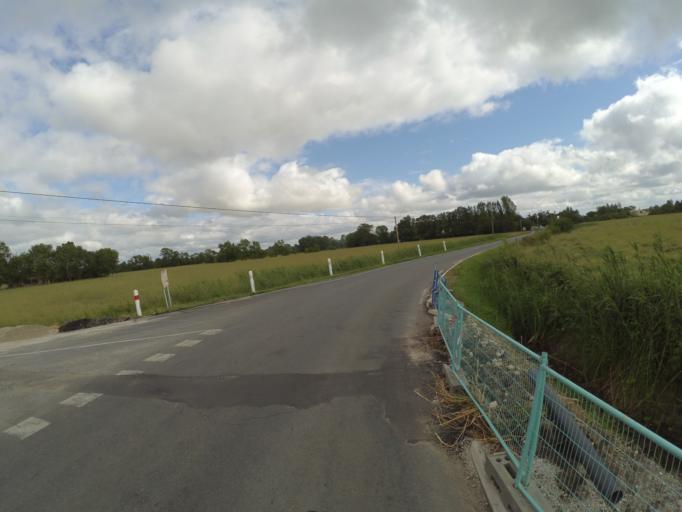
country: FR
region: Aquitaine
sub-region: Departement de la Gironde
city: Ludon-Medoc
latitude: 44.9878
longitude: -0.5767
